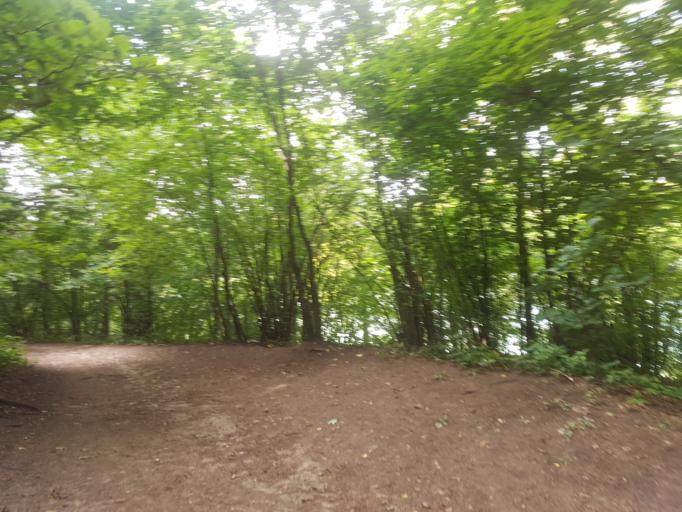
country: LT
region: Vilnius County
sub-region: Vilnius
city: Fabijoniskes
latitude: 54.7875
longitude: 25.3382
